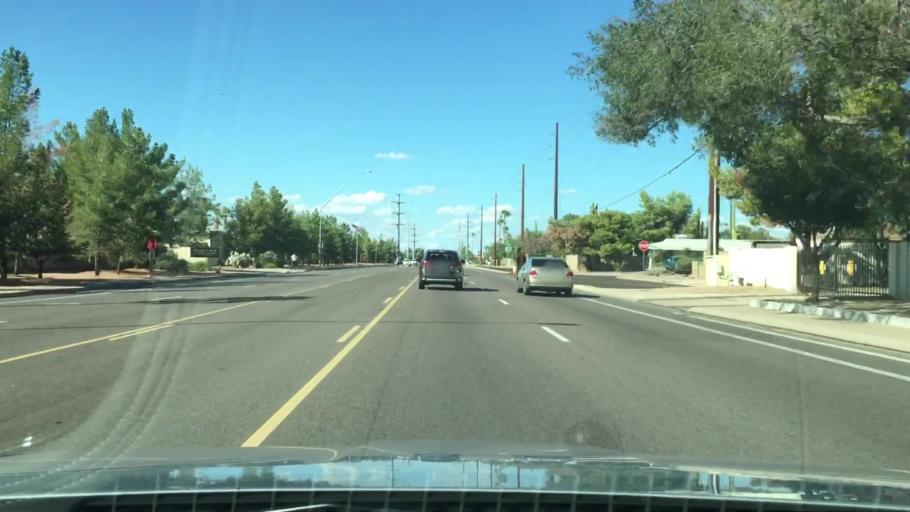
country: US
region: Arizona
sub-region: Maricopa County
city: Gilbert
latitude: 33.4189
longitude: -111.7191
